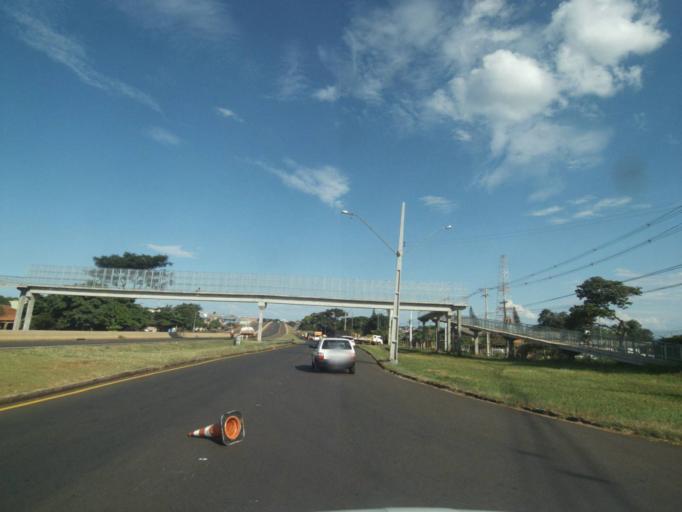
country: BR
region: Parana
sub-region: Londrina
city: Londrina
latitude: -23.3592
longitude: -51.1553
